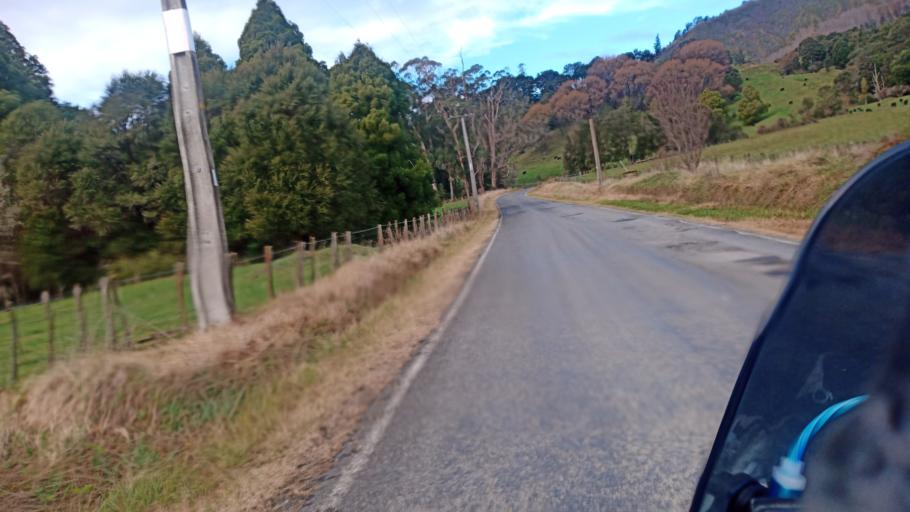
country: NZ
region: Gisborne
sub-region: Gisborne District
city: Gisborne
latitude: -38.4085
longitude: 177.9397
